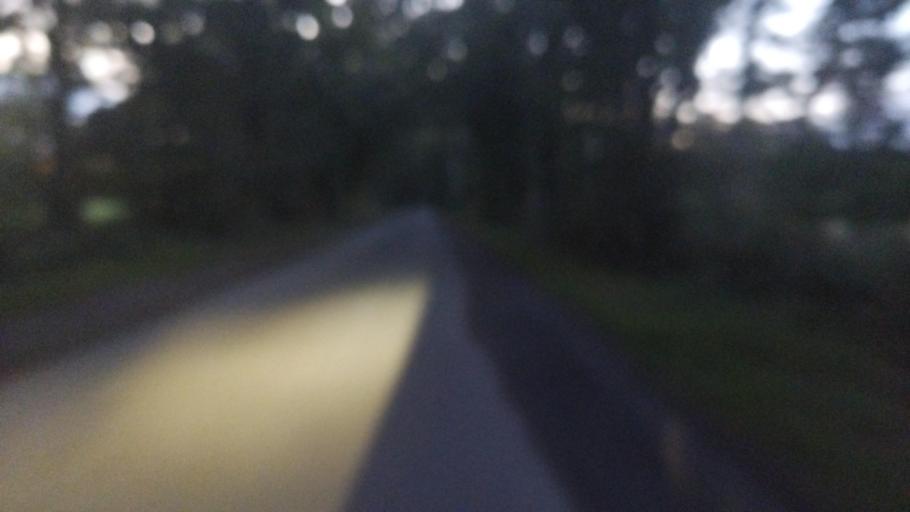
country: DE
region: North Rhine-Westphalia
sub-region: Regierungsbezirk Munster
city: Steinfurt
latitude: 52.1218
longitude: 7.3325
